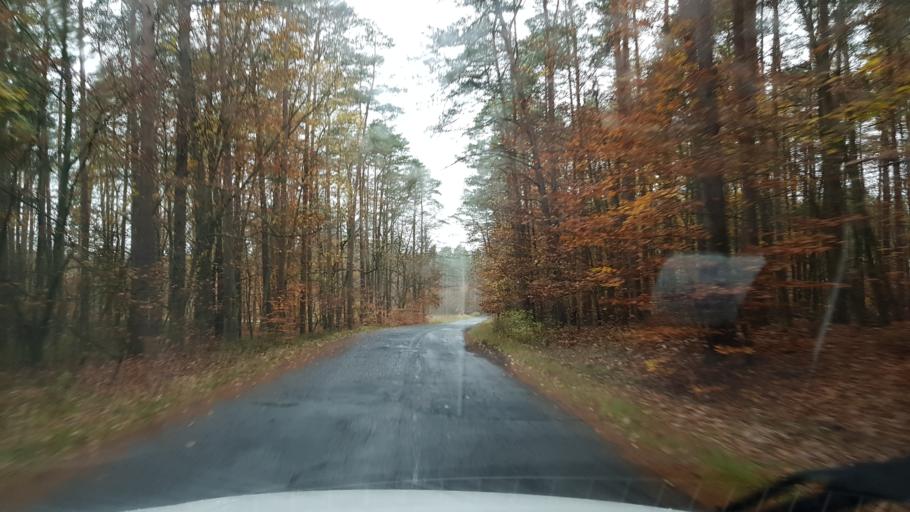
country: PL
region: West Pomeranian Voivodeship
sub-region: Powiat goleniowski
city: Stepnica
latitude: 53.6625
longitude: 14.7280
